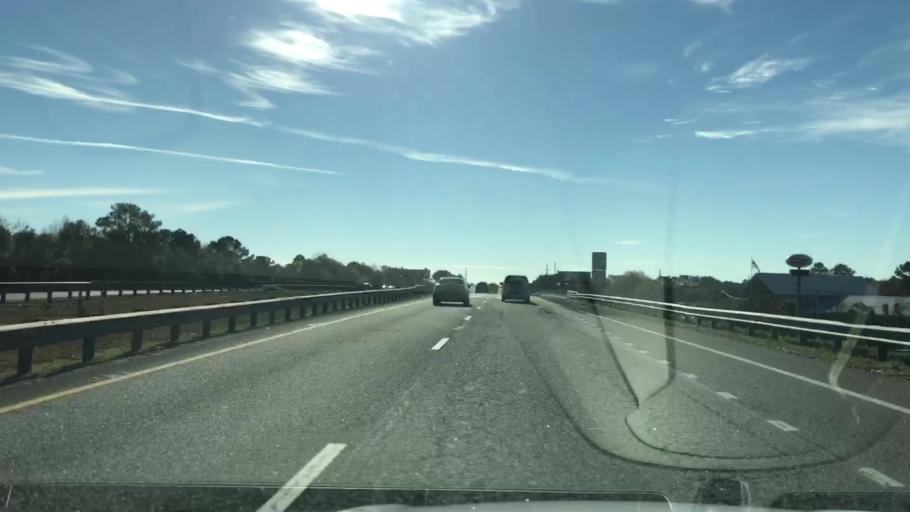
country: US
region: South Carolina
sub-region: Charleston County
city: North Charleston
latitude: 32.8635
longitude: -80.0264
